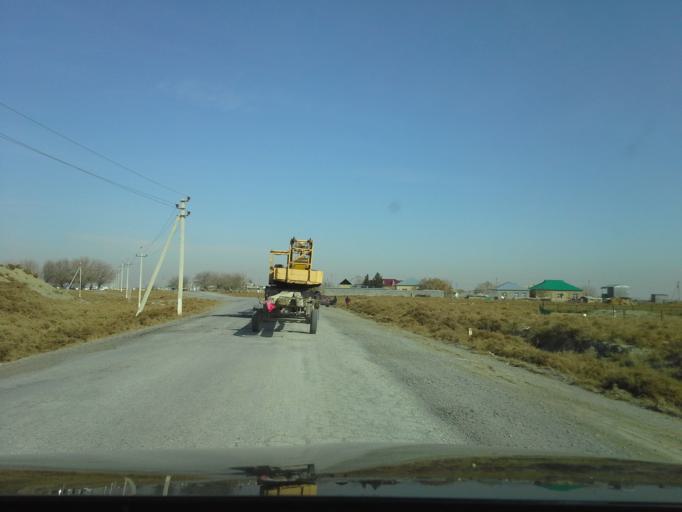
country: TM
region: Ahal
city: Abadan
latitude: 38.1149
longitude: 57.9924
